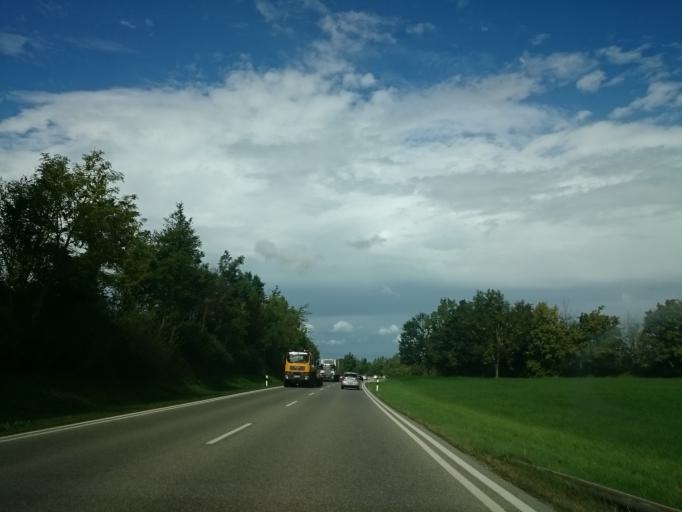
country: DE
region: Bavaria
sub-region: Swabia
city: Mauerstetten
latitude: 47.8720
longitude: 10.6497
